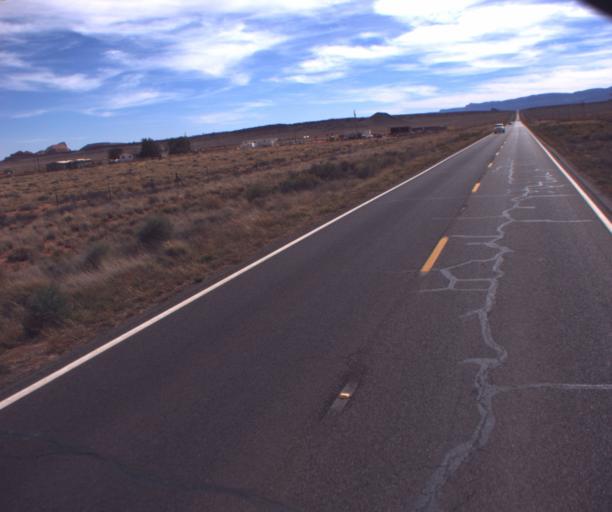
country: US
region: Arizona
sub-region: Navajo County
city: Kayenta
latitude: 36.7839
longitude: -110.2300
